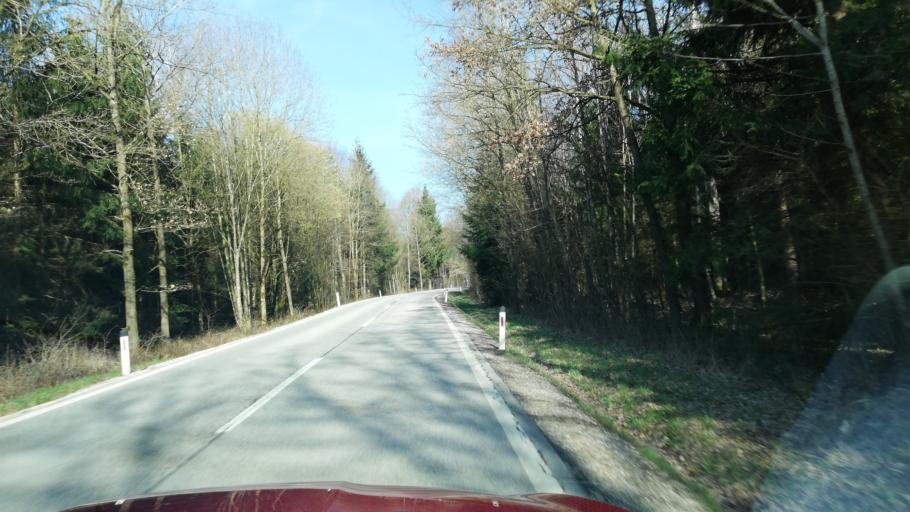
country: AT
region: Upper Austria
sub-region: Politischer Bezirk Kirchdorf an der Krems
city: Kremsmunster
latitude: 48.0815
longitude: 14.1158
